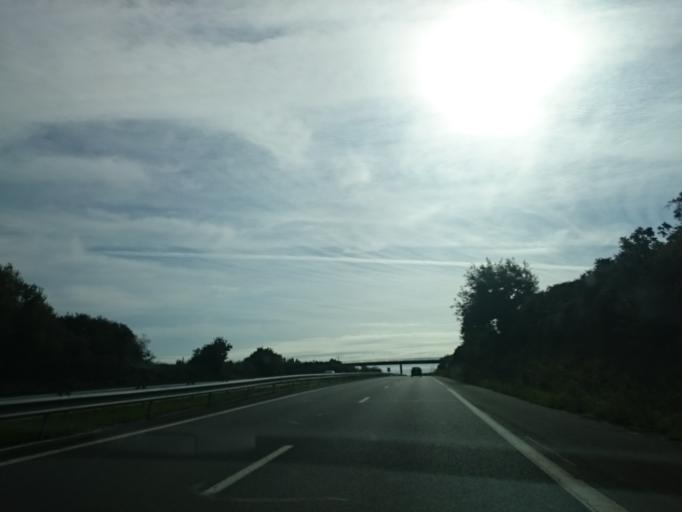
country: FR
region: Brittany
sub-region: Departement du Morbihan
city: Muzillac
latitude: 47.5459
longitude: -2.4388
